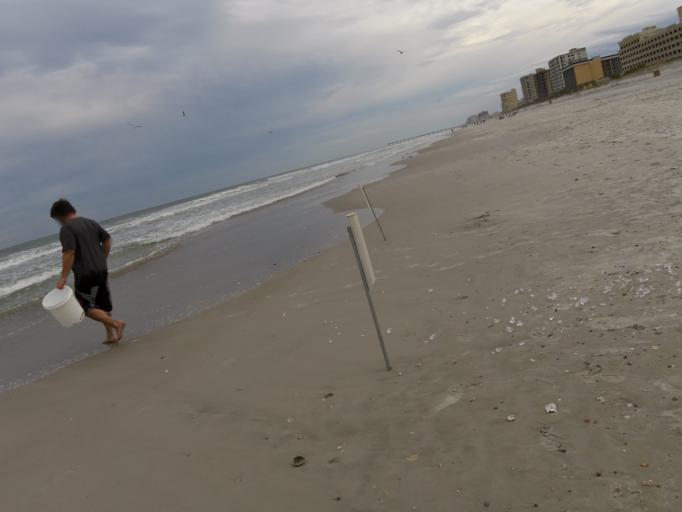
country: US
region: Florida
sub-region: Duval County
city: Neptune Beach
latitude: 30.3063
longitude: -81.3915
